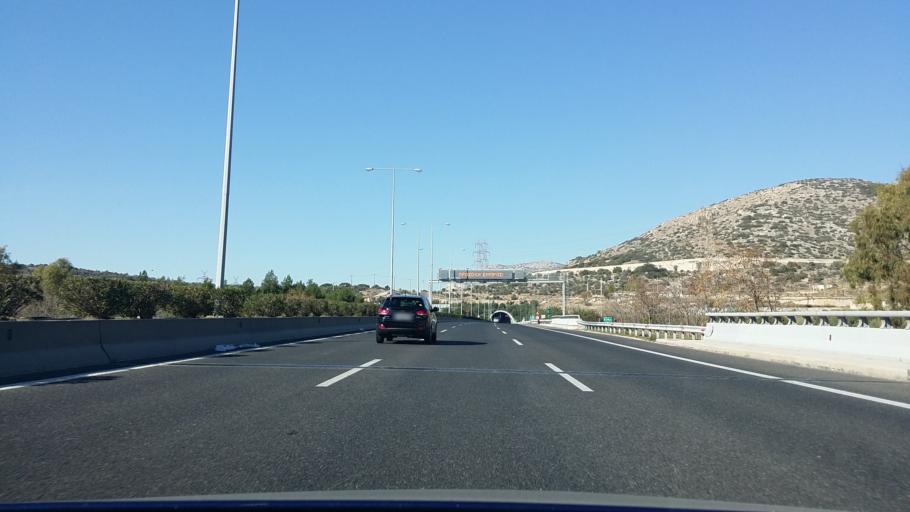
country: GR
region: Attica
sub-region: Nomarchia Dytikis Attikis
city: Ano Liosia
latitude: 38.0786
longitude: 23.6781
